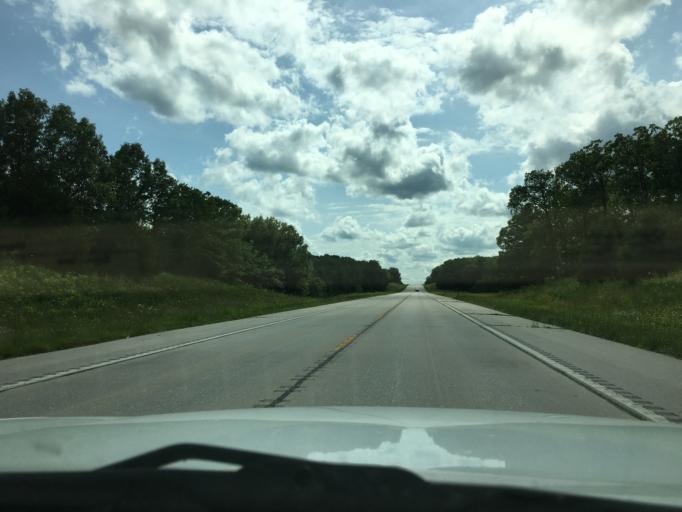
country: US
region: Missouri
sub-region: Franklin County
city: Gerald
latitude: 38.4212
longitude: -91.2851
